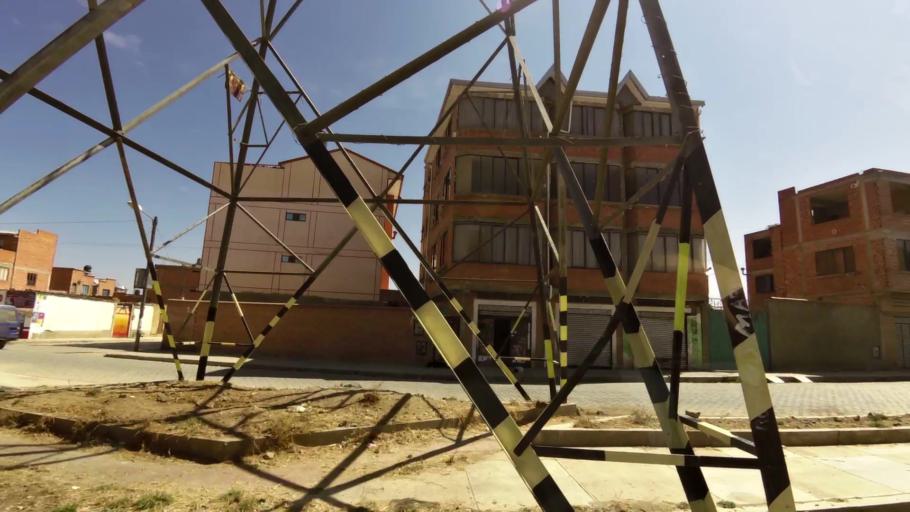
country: BO
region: La Paz
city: La Paz
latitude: -16.5373
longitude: -68.1548
